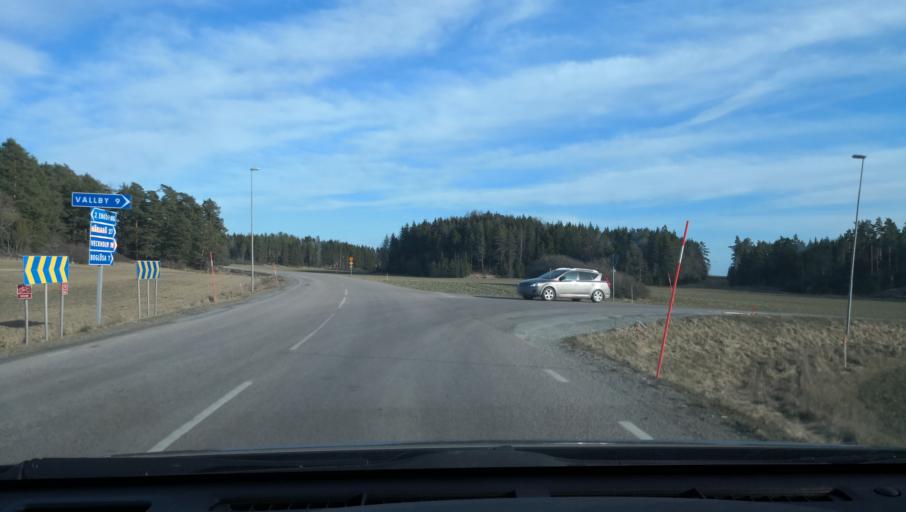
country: SE
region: Uppsala
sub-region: Enkopings Kommun
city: Enkoping
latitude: 59.6223
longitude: 17.0988
